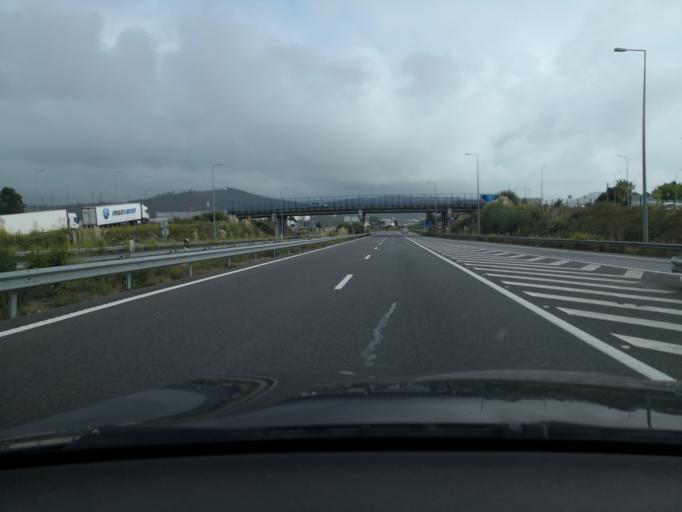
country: PT
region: Porto
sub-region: Valongo
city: Alfena
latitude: 41.2332
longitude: -8.5387
